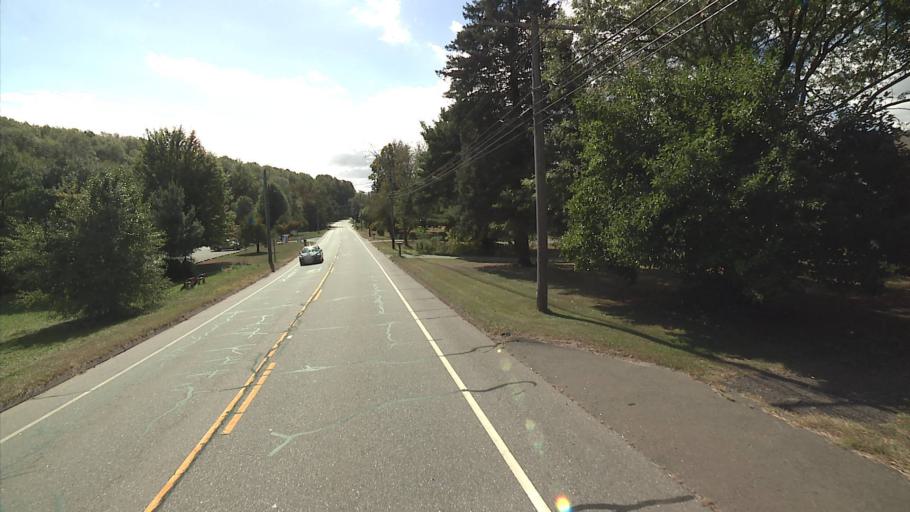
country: US
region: Connecticut
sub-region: Middlesex County
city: Durham
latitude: 41.5228
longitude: -72.7290
